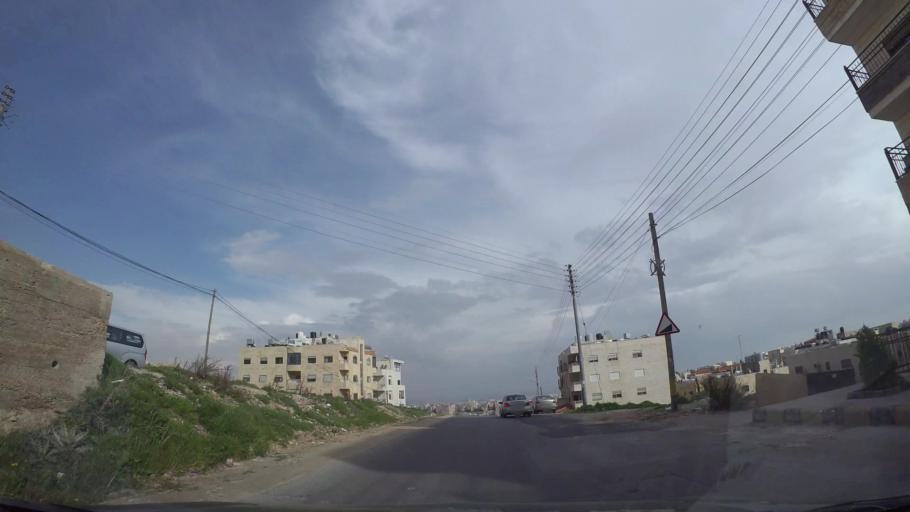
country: JO
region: Amman
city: Amman
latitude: 32.0109
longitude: 35.9382
